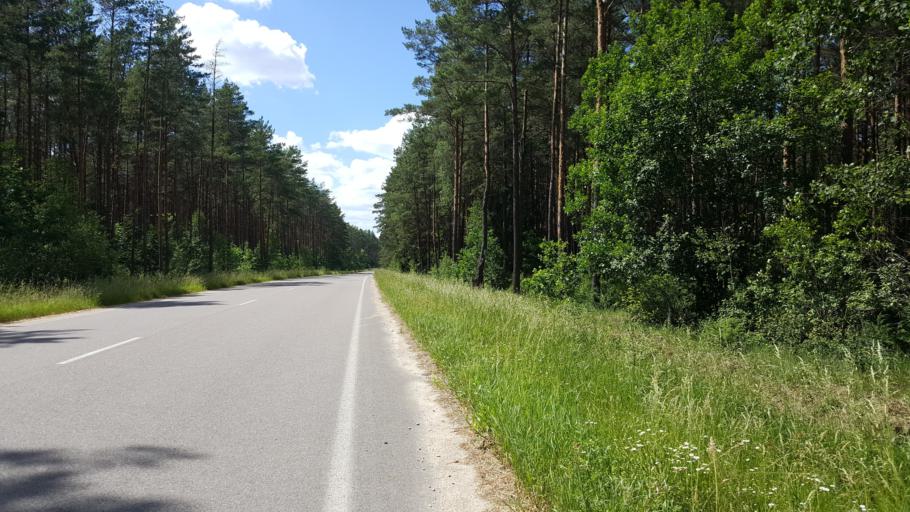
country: PL
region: Podlasie
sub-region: Powiat hajnowski
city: Czeremcha
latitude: 52.5407
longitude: 23.5193
